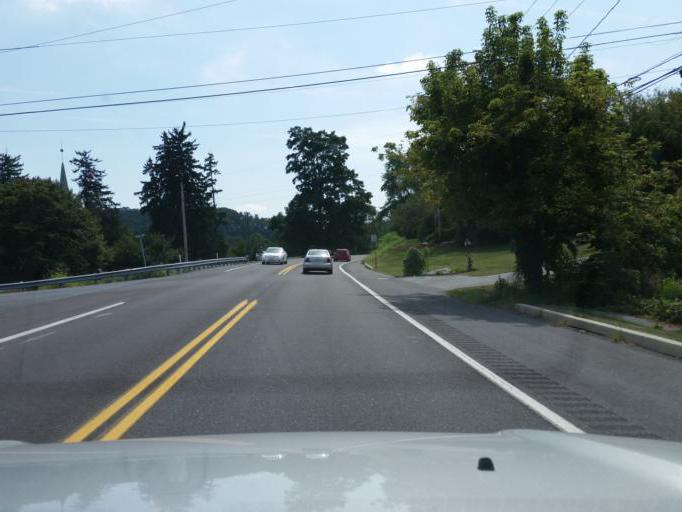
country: US
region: Pennsylvania
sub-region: Dauphin County
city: Hummelstown
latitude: 40.2460
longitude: -76.7066
